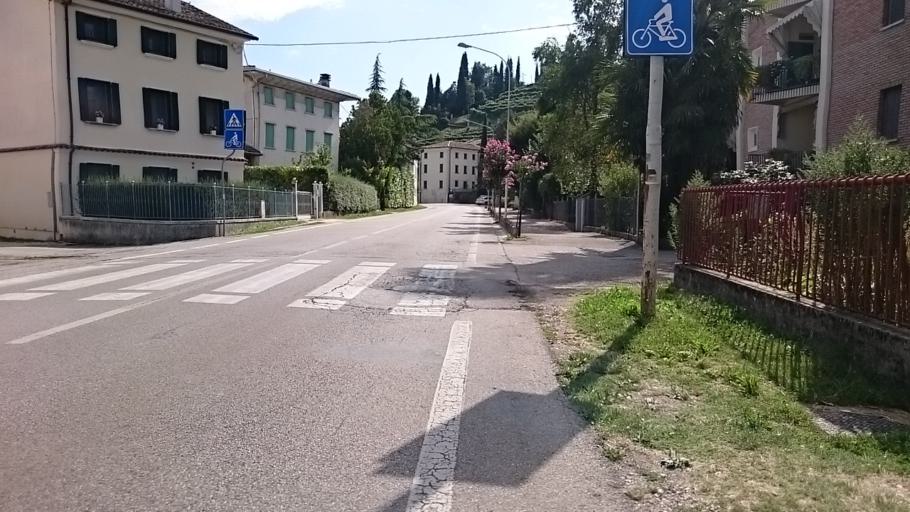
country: IT
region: Veneto
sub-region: Provincia di Treviso
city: Vidor
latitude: 45.8645
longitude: 12.0397
